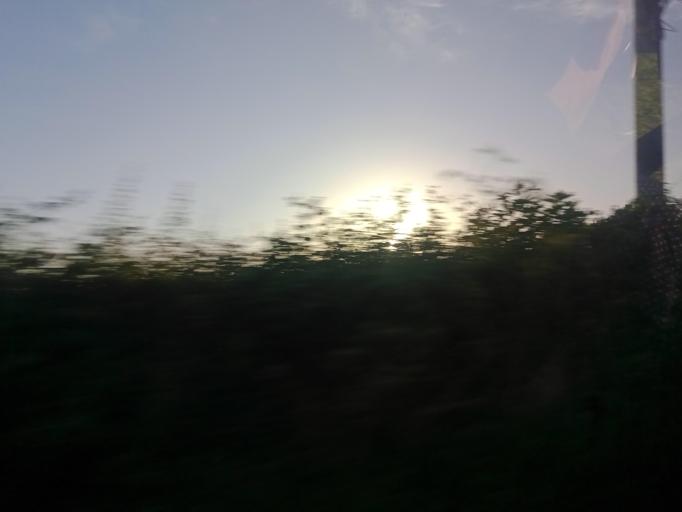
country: IE
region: Leinster
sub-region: Kilkenny
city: Castlecomer
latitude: 52.7335
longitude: -7.2365
